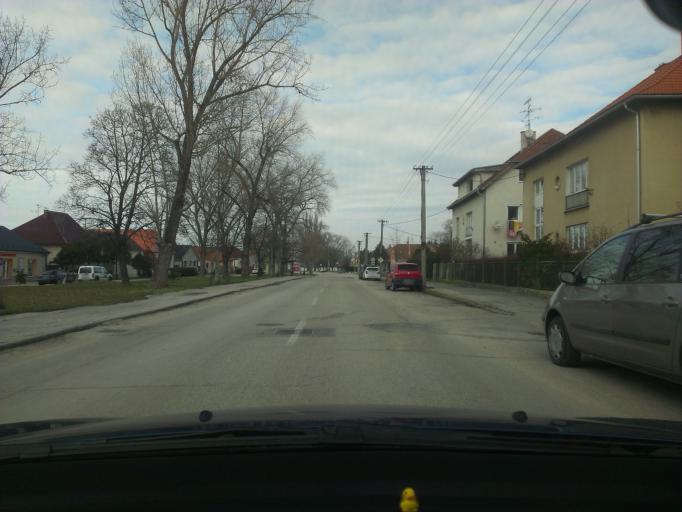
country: SK
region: Trnavsky
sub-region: Okres Trnava
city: Piestany
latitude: 48.6035
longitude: 17.8338
